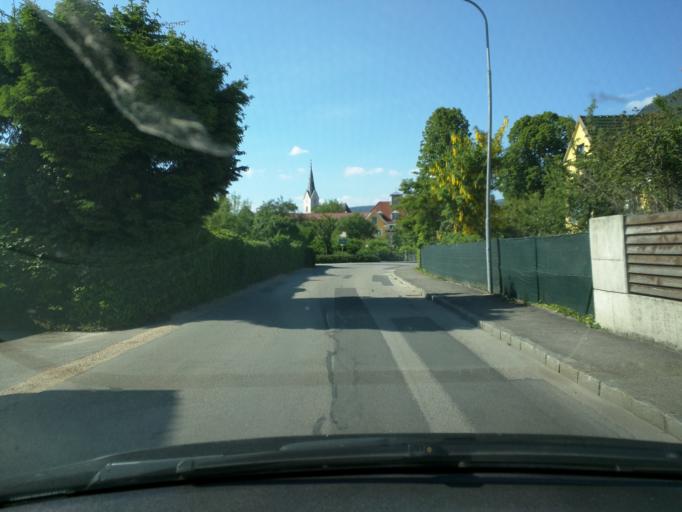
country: AT
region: Lower Austria
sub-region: Politischer Bezirk Melk
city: Ybbs an der Donau
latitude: 48.1750
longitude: 15.0869
